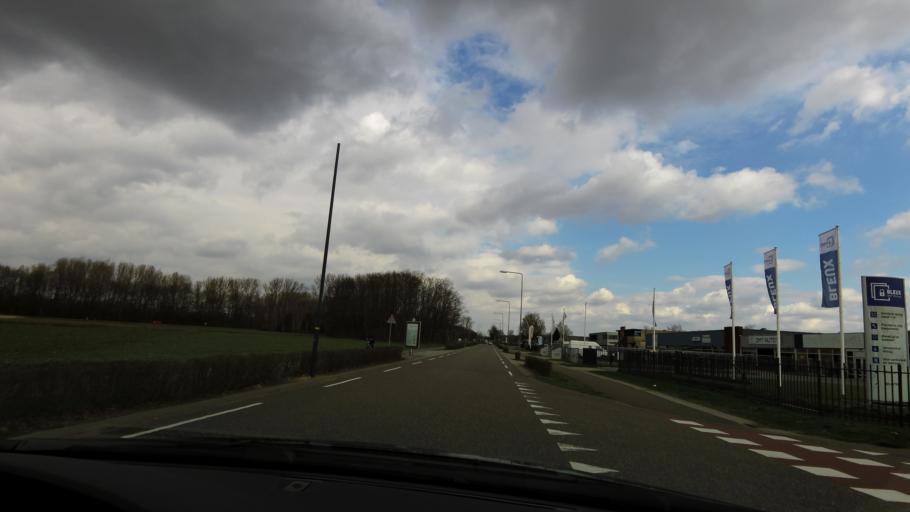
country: NL
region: Limburg
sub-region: Gemeente Sittard-Geleen
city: Limbricht
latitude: 51.0708
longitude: 5.8611
